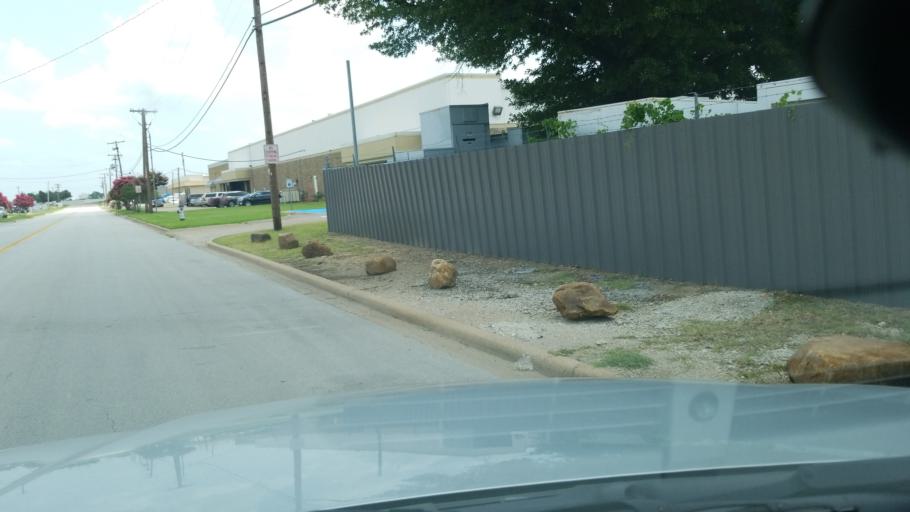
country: US
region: Texas
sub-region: Dallas County
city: Irving
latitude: 32.8184
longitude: -96.9154
